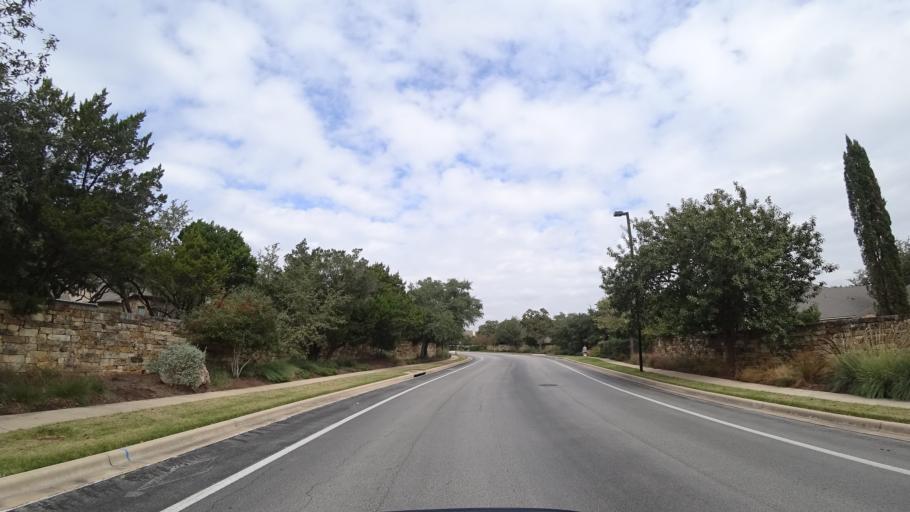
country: US
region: Texas
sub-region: Travis County
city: Shady Hollow
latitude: 30.1892
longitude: -97.9064
